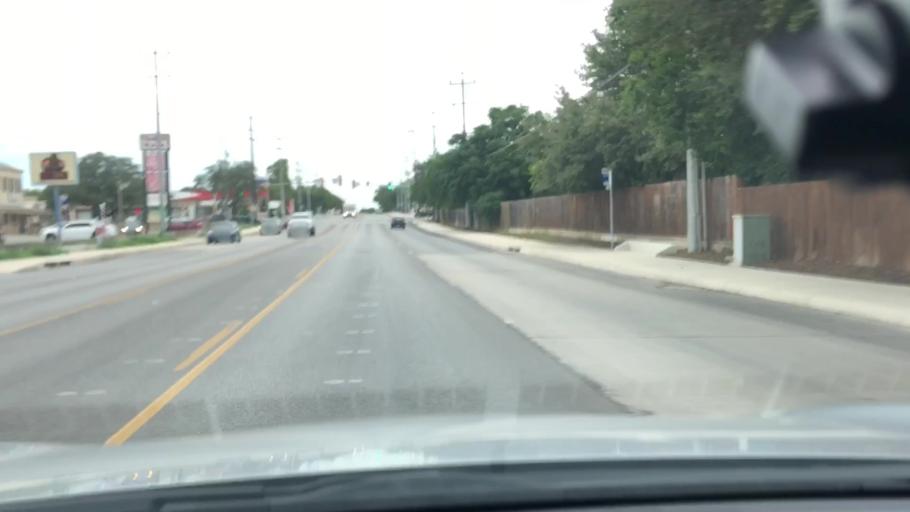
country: US
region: Texas
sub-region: Bexar County
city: Leon Valley
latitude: 29.4889
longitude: -98.6656
